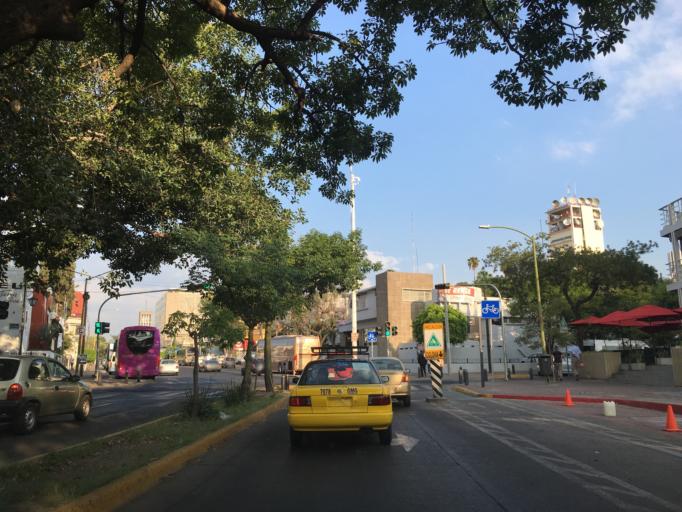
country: MX
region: Jalisco
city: Guadalajara
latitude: 20.6723
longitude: -103.3658
